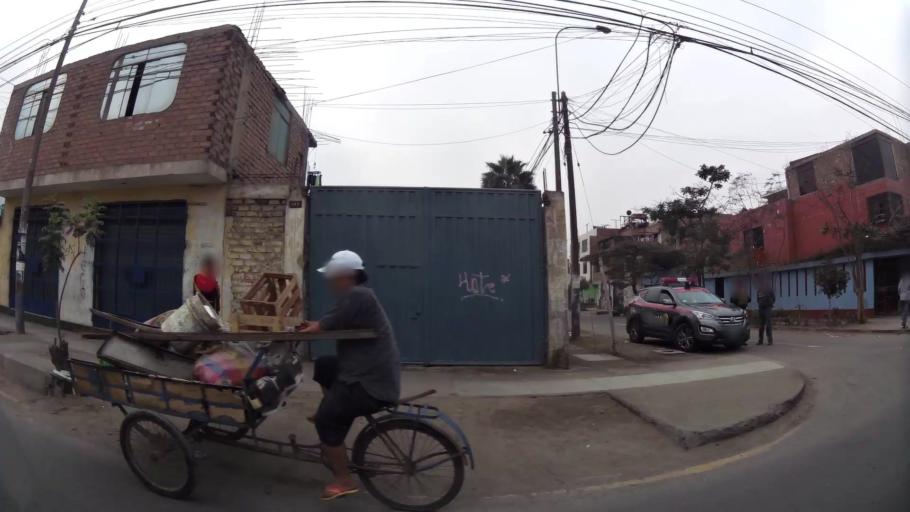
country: PE
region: Lima
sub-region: Lima
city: Independencia
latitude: -11.9753
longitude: -77.0079
